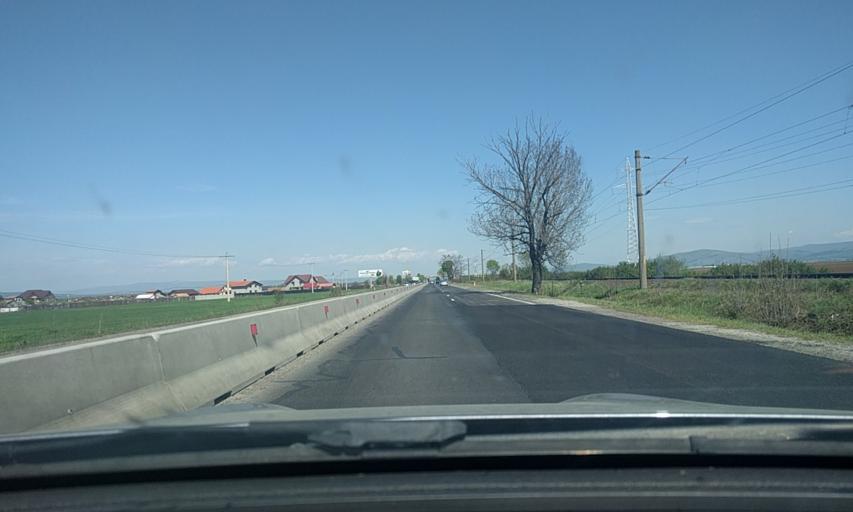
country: RO
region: Brasov
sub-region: Comuna Harman
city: Harman
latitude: 45.7059
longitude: 25.6985
